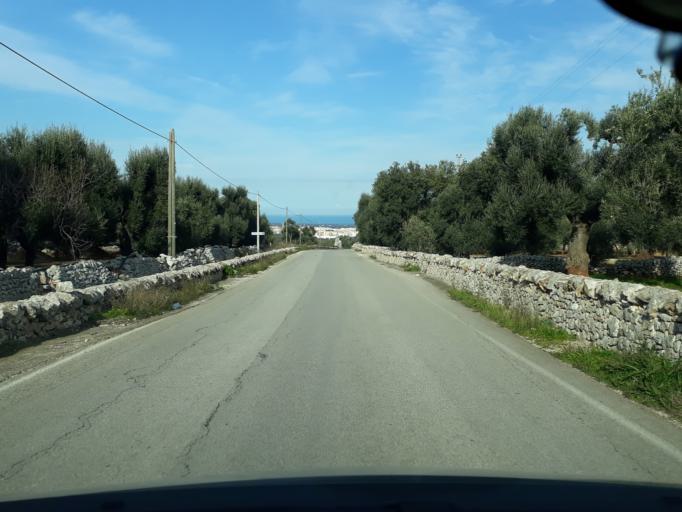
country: IT
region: Apulia
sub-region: Provincia di Brindisi
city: Lamie di Olimpie-Selva
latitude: 40.8105
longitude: 17.3552
